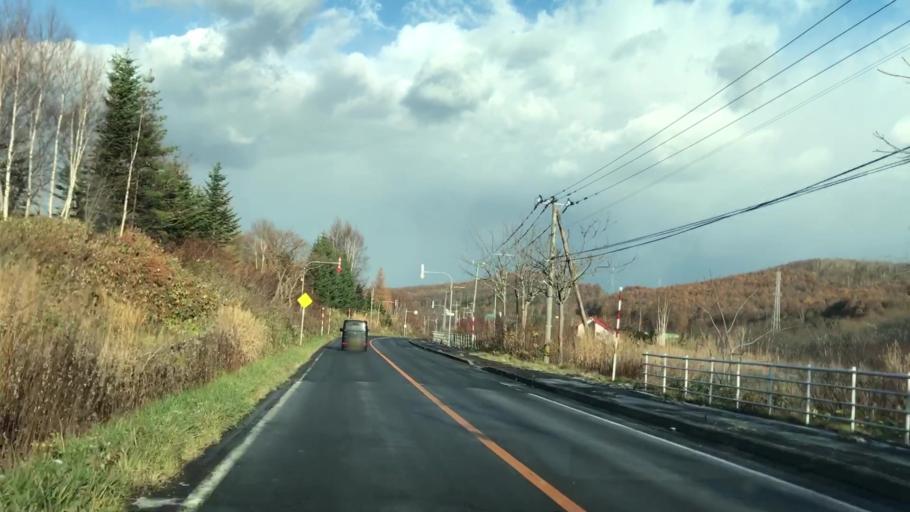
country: JP
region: Hokkaido
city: Otaru
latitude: 43.1888
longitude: 140.9595
